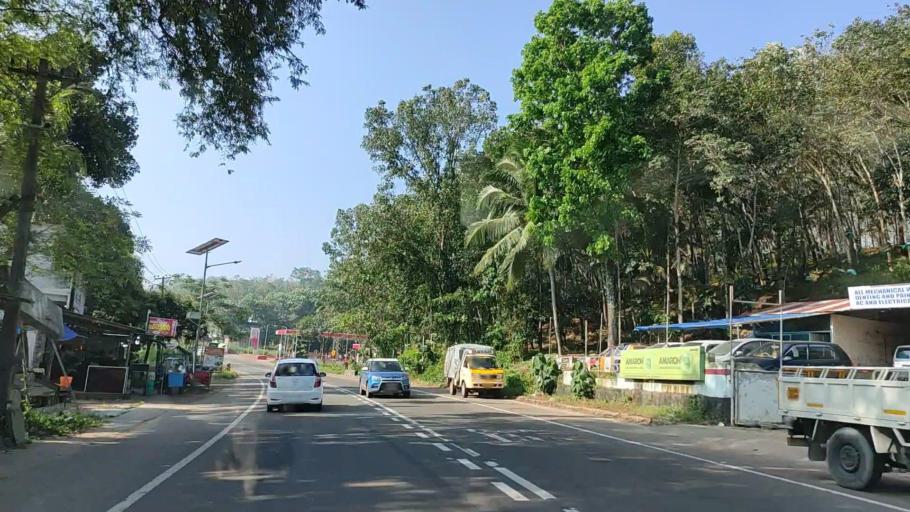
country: IN
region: Kerala
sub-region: Kollam
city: Punalur
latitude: 8.9176
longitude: 76.8544
